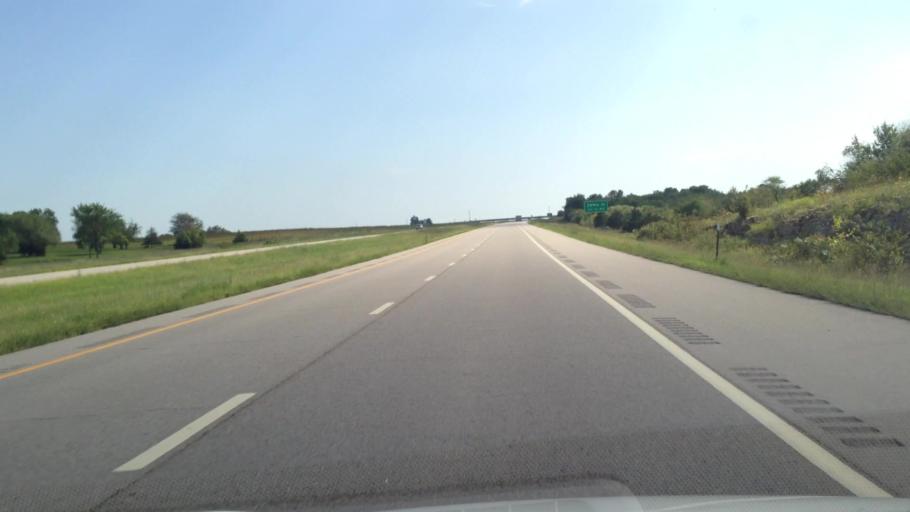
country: US
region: Kansas
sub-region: Linn County
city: La Cygne
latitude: 38.4139
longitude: -94.6879
